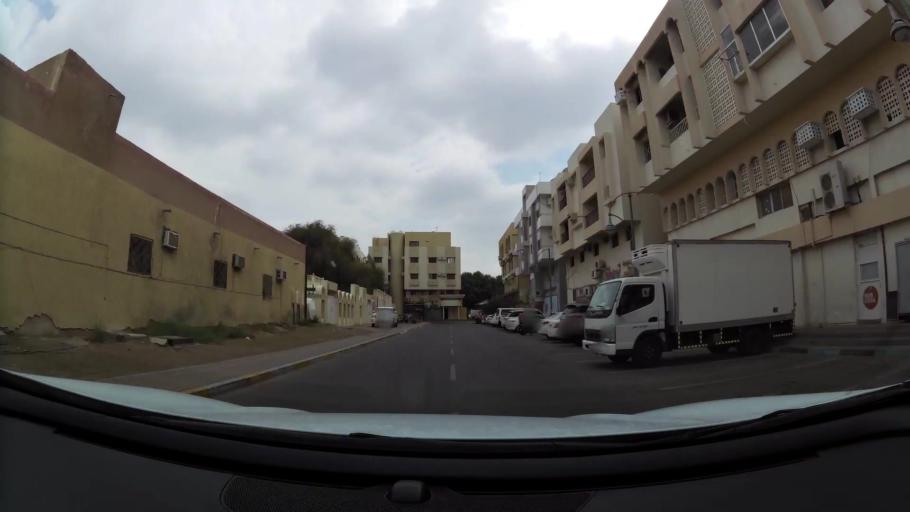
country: AE
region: Abu Dhabi
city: Al Ain
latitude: 24.2261
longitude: 55.7638
